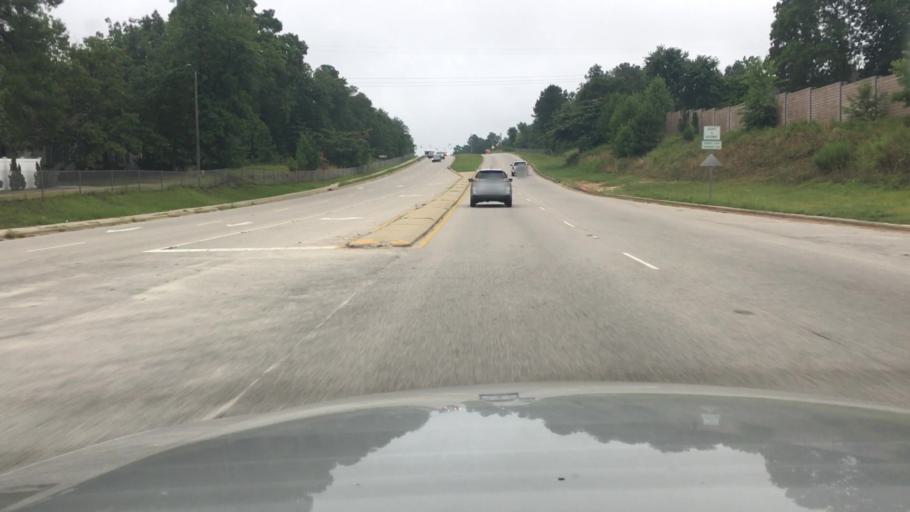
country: US
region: North Carolina
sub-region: Cumberland County
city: Hope Mills
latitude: 34.9866
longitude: -78.9341
